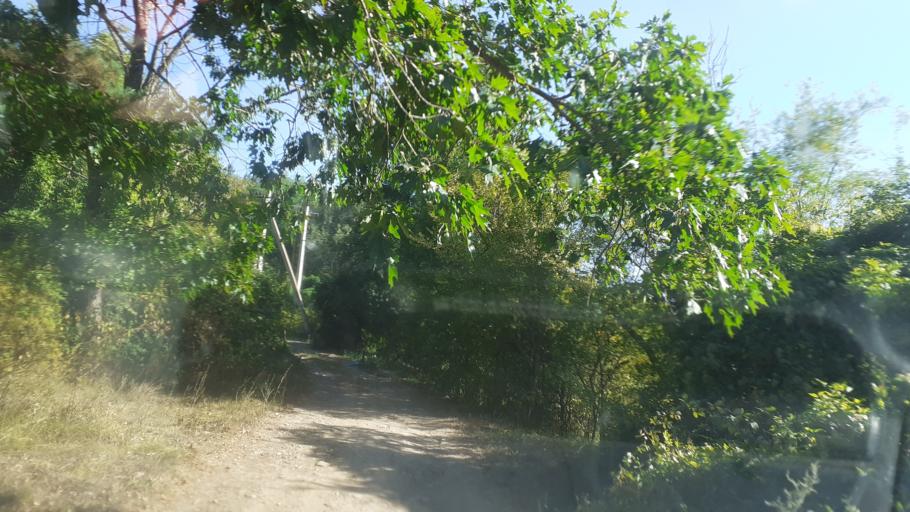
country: RU
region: Krasnodarskiy
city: Azovskaya
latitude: 44.7230
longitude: 38.5344
